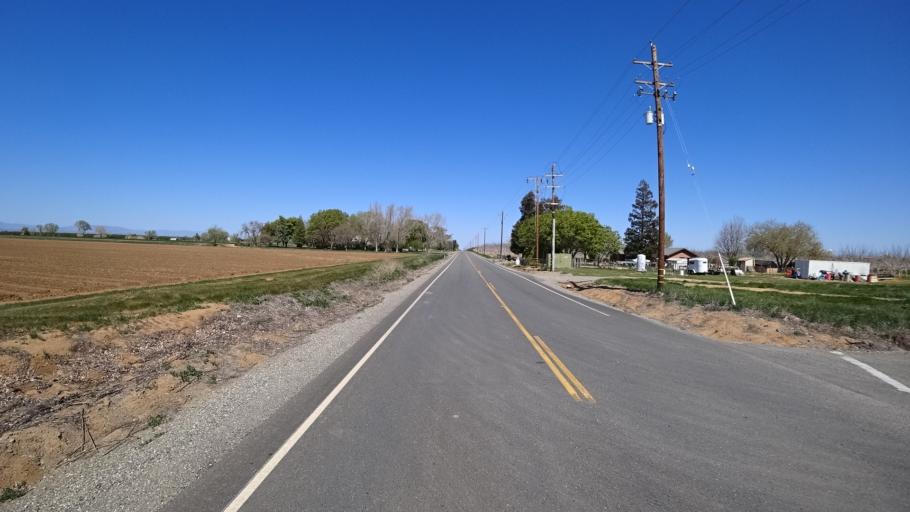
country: US
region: California
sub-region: Glenn County
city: Willows
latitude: 39.5096
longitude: -122.2492
